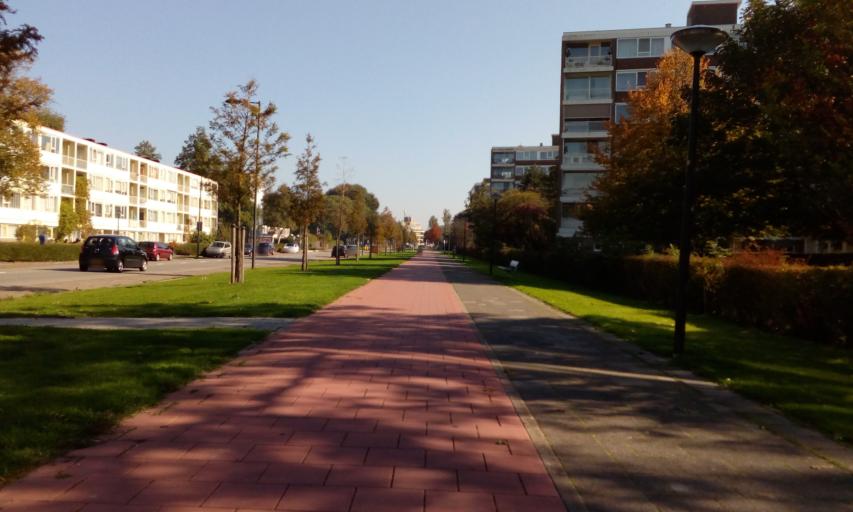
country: NL
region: South Holland
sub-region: Gemeente Vlaardingen
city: Vlaardingen
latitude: 51.9133
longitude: 4.3224
